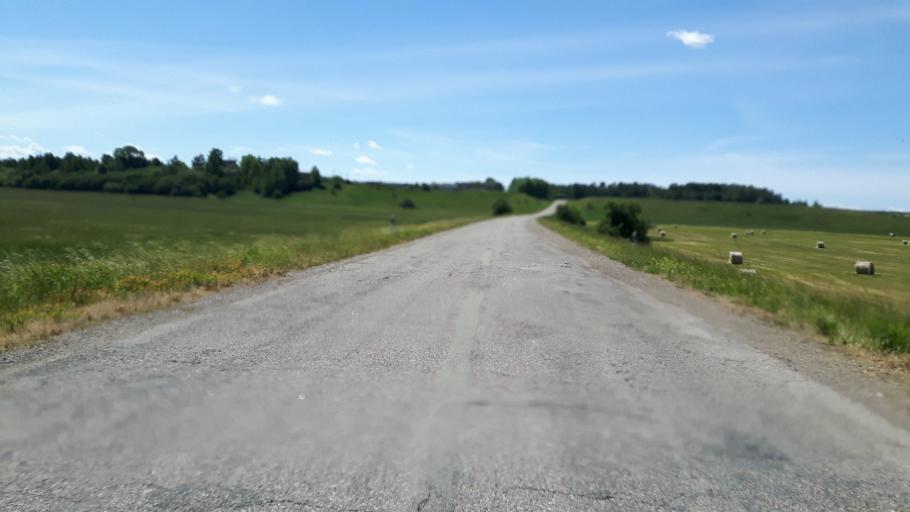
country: LV
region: Kandava
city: Kandava
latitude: 57.0389
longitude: 22.8970
